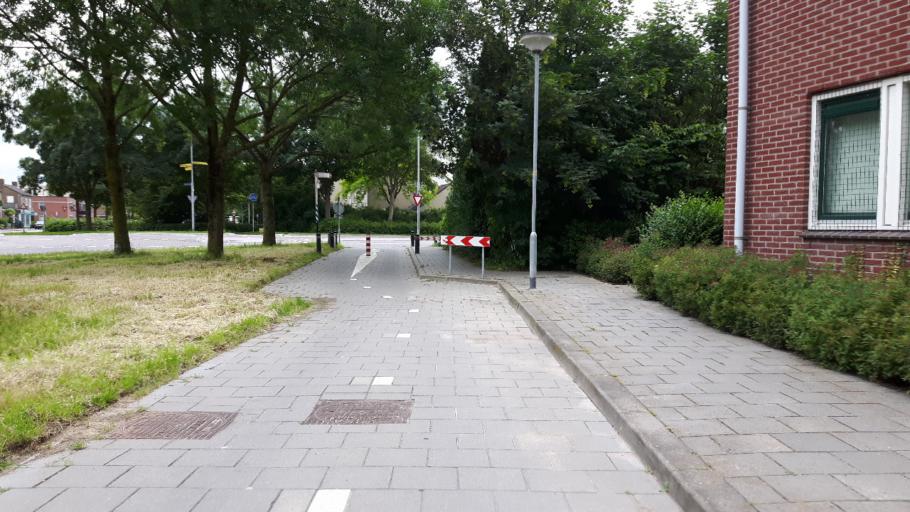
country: NL
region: Utrecht
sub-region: Stichtse Vecht
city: Vreeland
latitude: 52.2526
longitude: 5.0491
